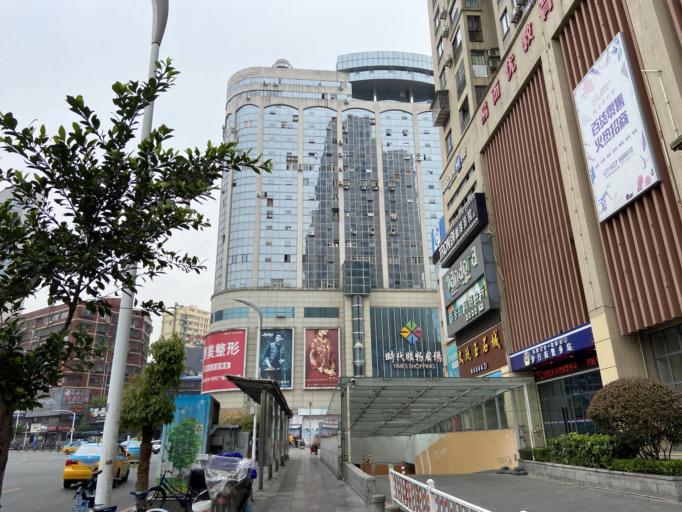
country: CN
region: Hubei
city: Yichang
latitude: 30.6998
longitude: 111.2785
